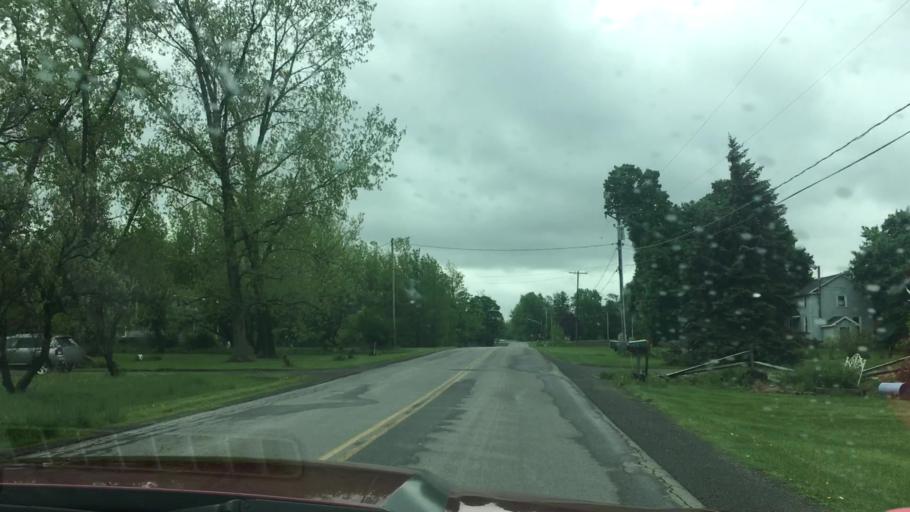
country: US
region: New York
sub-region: Genesee County
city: Batavia
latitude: 43.0761
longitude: -78.1396
